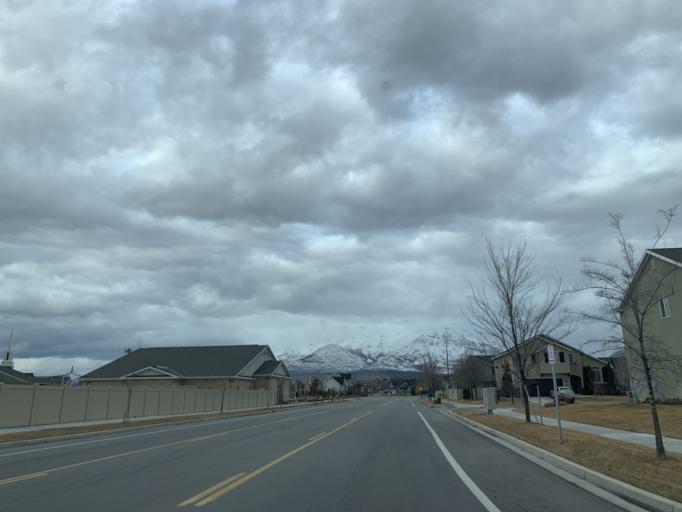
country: US
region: Utah
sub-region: Utah County
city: Orem
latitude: 40.2512
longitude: -111.7138
